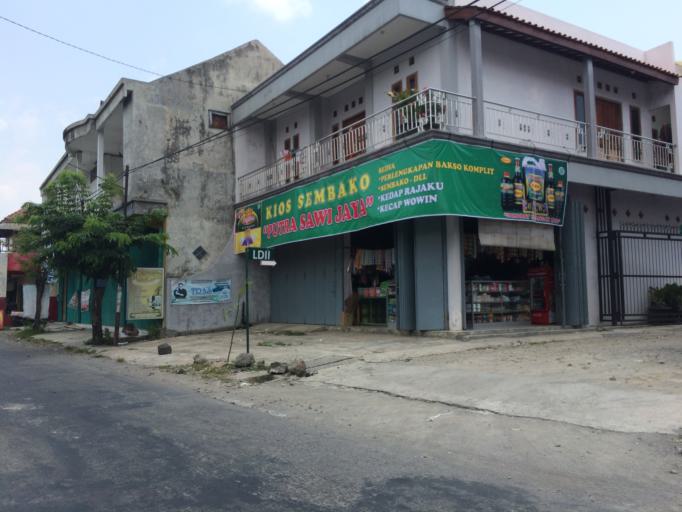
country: ID
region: Central Java
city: Grogol
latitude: -7.6154
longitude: 110.8201
